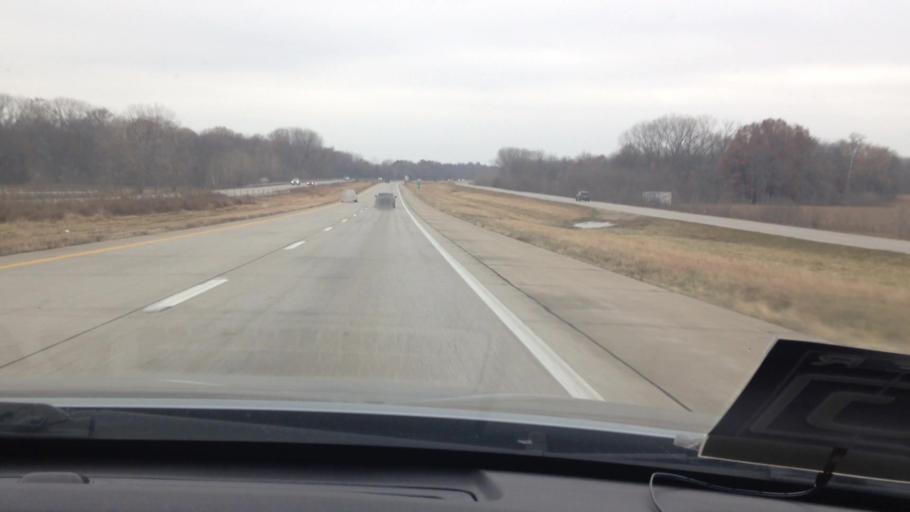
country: US
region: Missouri
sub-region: Cass County
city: Harrisonville
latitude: 38.6646
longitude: -94.3930
